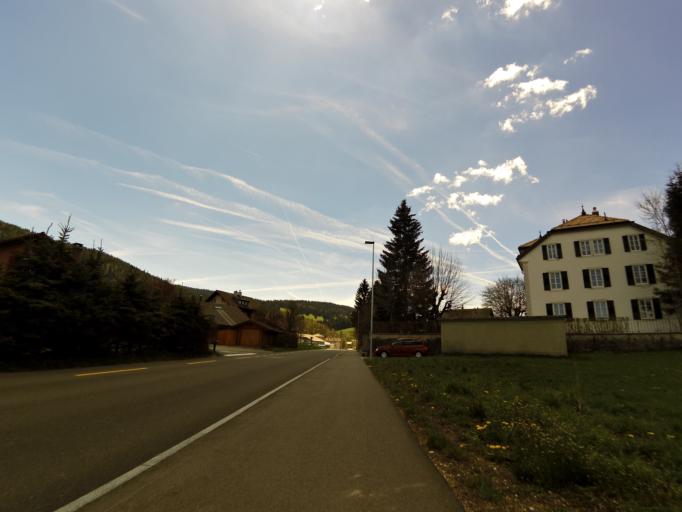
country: CH
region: Vaud
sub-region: Jura-Nord vaudois District
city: Le Chenit
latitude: 46.5879
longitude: 6.2142
